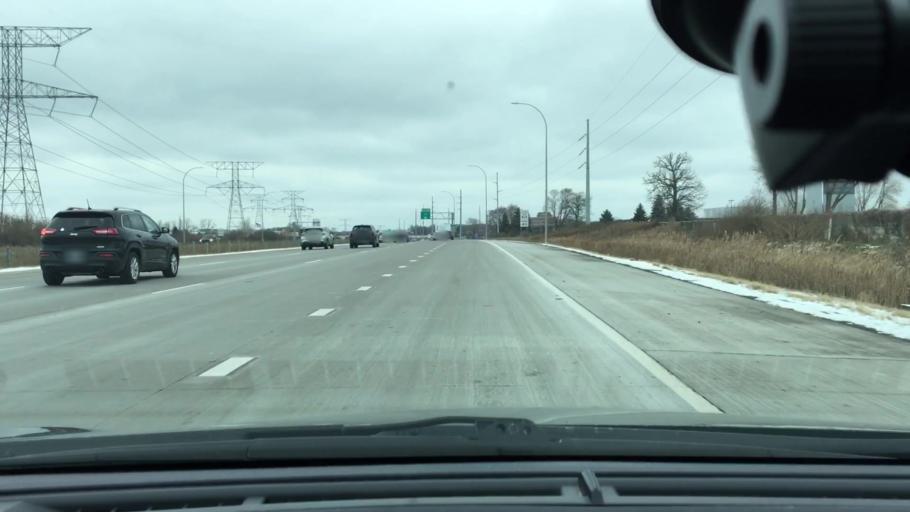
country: US
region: Minnesota
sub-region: Hennepin County
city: Plymouth
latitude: 45.0011
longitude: -93.4573
